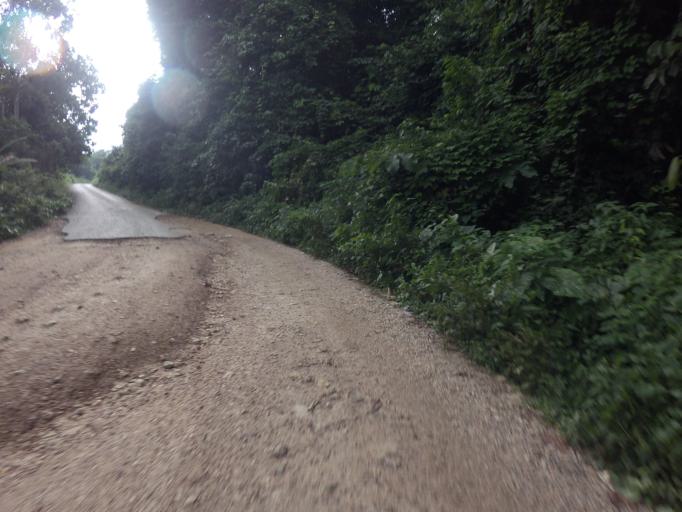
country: GH
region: Volta
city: Kpandu
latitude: 6.8256
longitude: 0.4258
